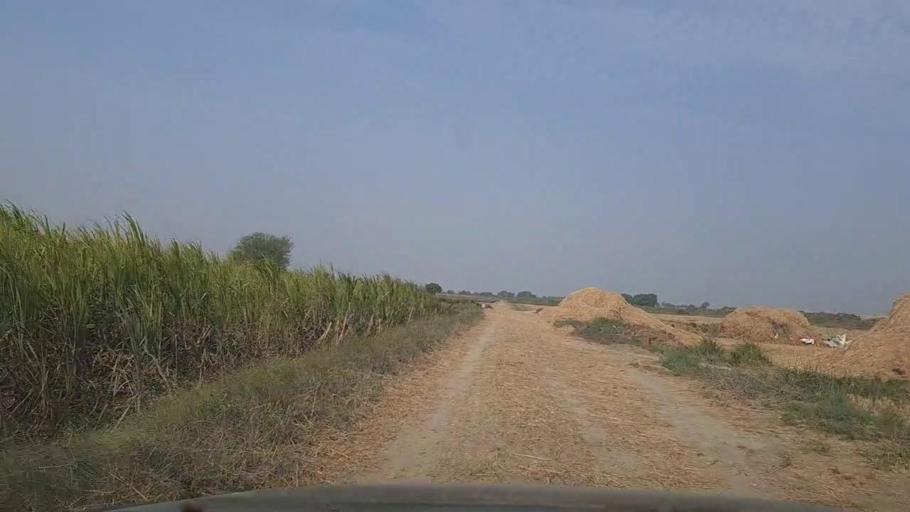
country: PK
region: Sindh
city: Bulri
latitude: 25.0161
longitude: 68.2837
